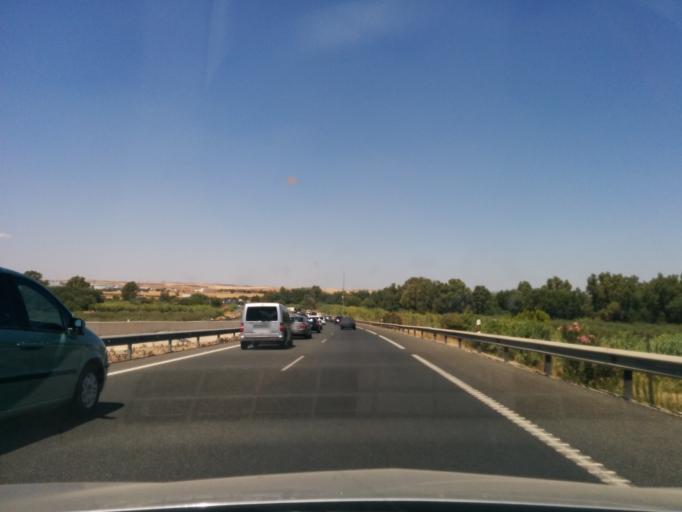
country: ES
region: Andalusia
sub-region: Provincia de Sevilla
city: Sanlucar la Mayor
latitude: 37.3705
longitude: -6.2217
